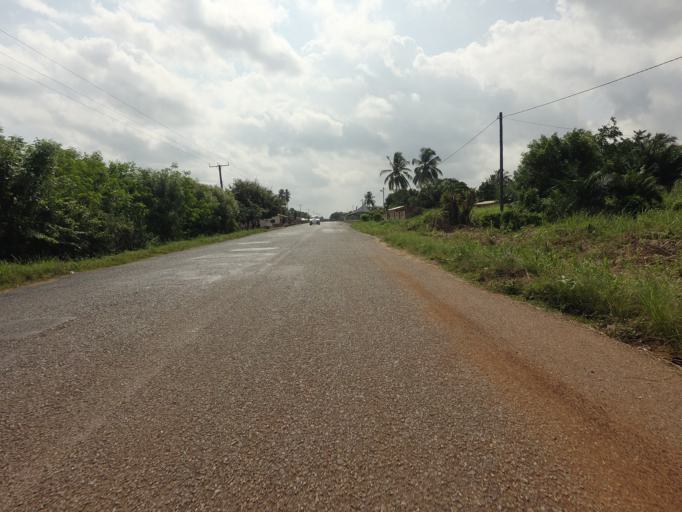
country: GH
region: Volta
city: Ho
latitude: 6.4128
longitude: 0.7587
